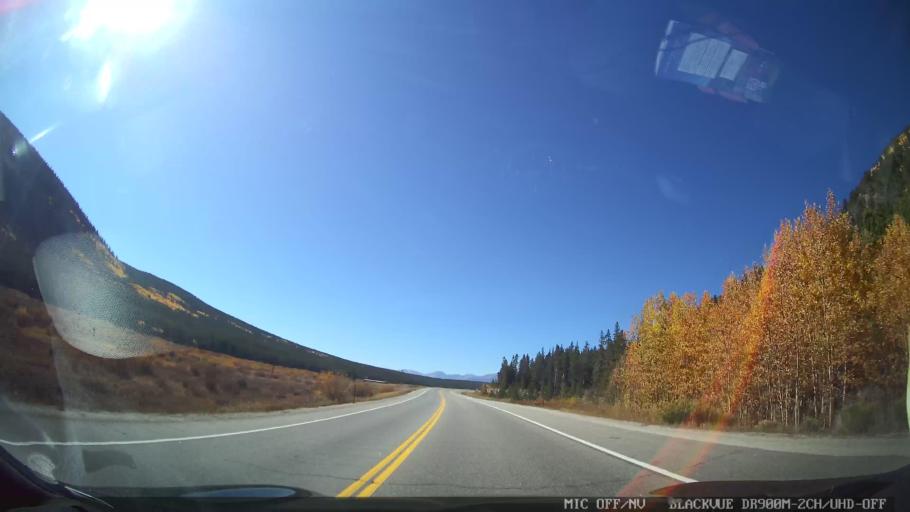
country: US
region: Colorado
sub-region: Lake County
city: Leadville North
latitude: 39.2949
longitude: -106.2744
